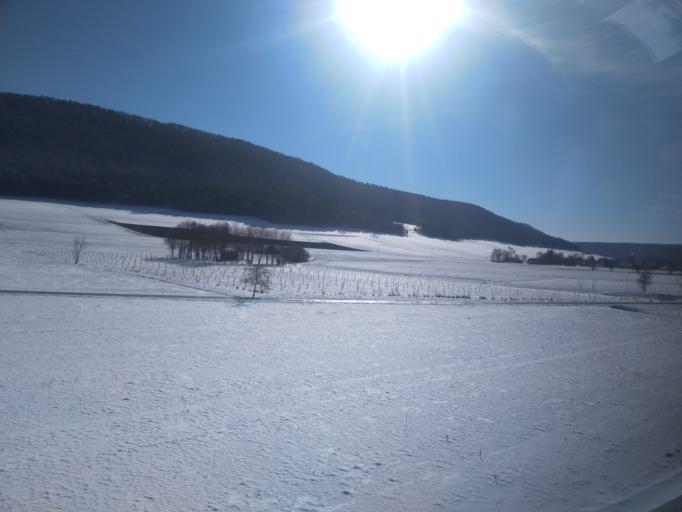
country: DE
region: Baden-Wuerttemberg
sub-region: Freiburg Region
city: Rietheim-Weilheim
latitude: 48.0340
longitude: 8.7780
